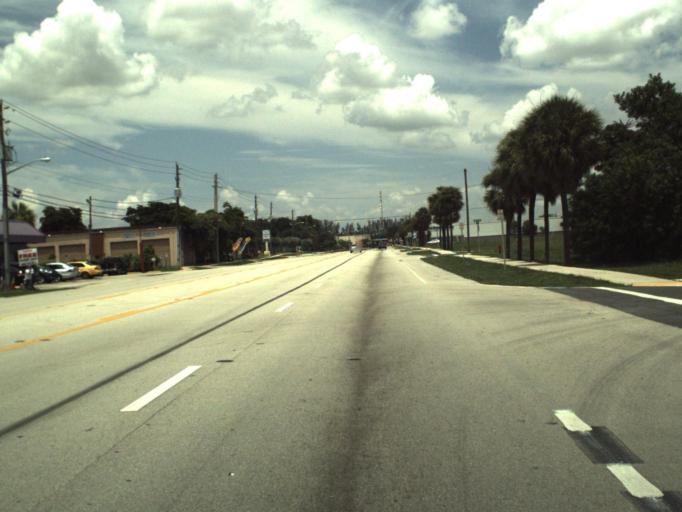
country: US
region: Florida
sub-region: Broward County
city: Coconut Creek
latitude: 26.2352
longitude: -80.1655
